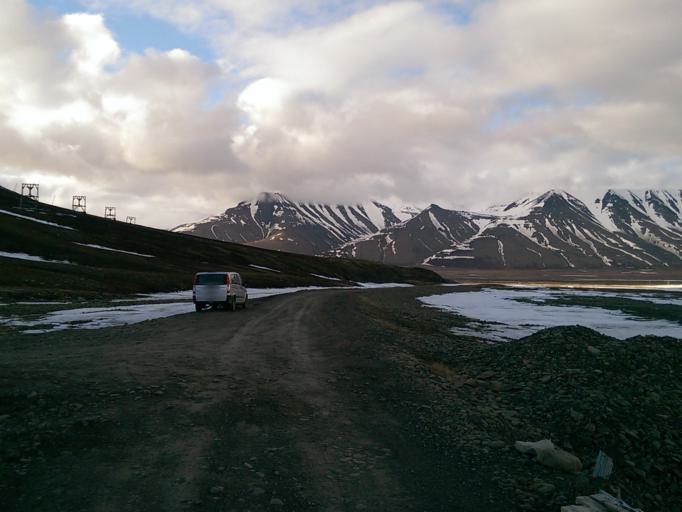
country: SJ
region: Svalbard
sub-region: Spitsbergen
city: Longyearbyen
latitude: 78.1855
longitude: 15.7629
